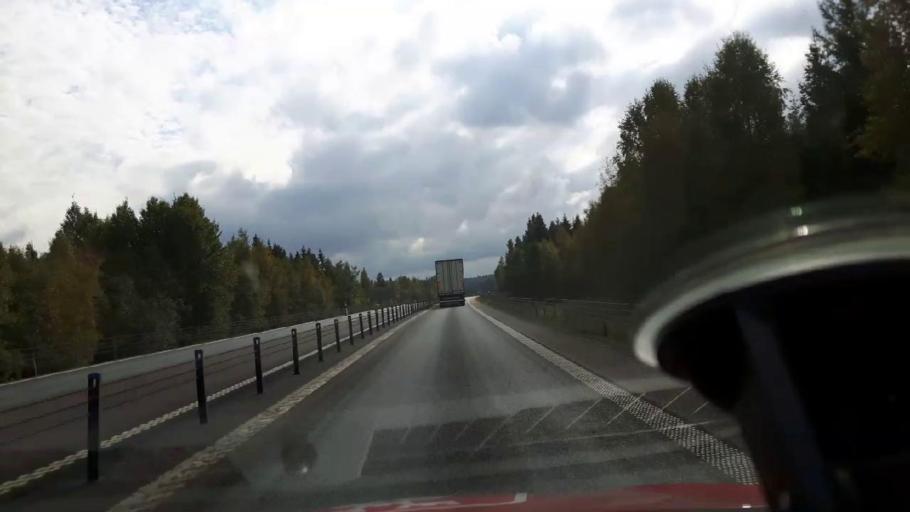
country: SE
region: Gaevleborg
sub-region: Gavle Kommun
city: Norrsundet
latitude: 60.9165
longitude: 17.0138
